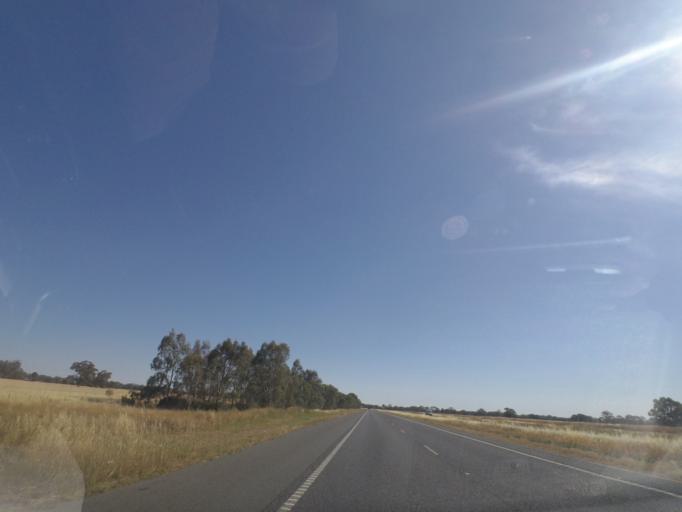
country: AU
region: Victoria
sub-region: Greater Shepparton
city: Shepparton
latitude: -36.6313
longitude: 145.2952
